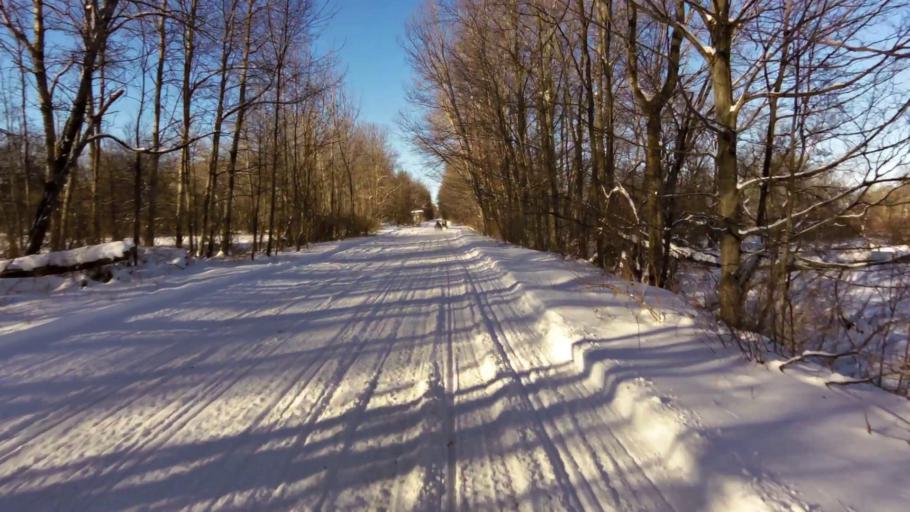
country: US
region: New York
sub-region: Chautauqua County
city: Mayville
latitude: 42.2645
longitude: -79.4942
